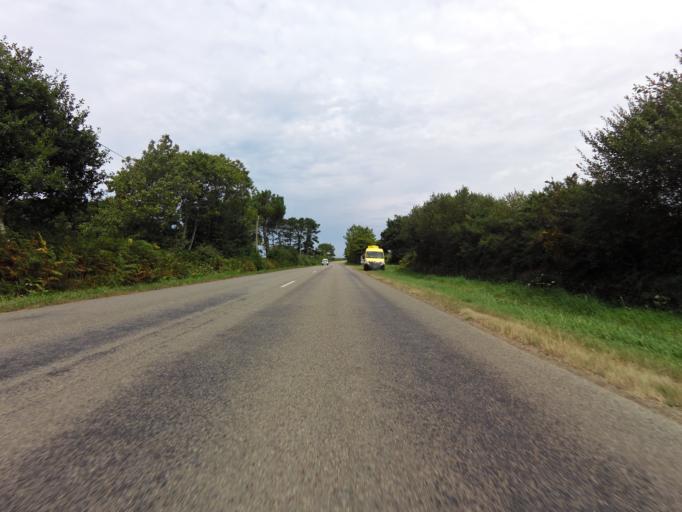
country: FR
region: Brittany
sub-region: Departement du Finistere
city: Poullan-sur-Mer
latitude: 48.0794
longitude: -4.4403
